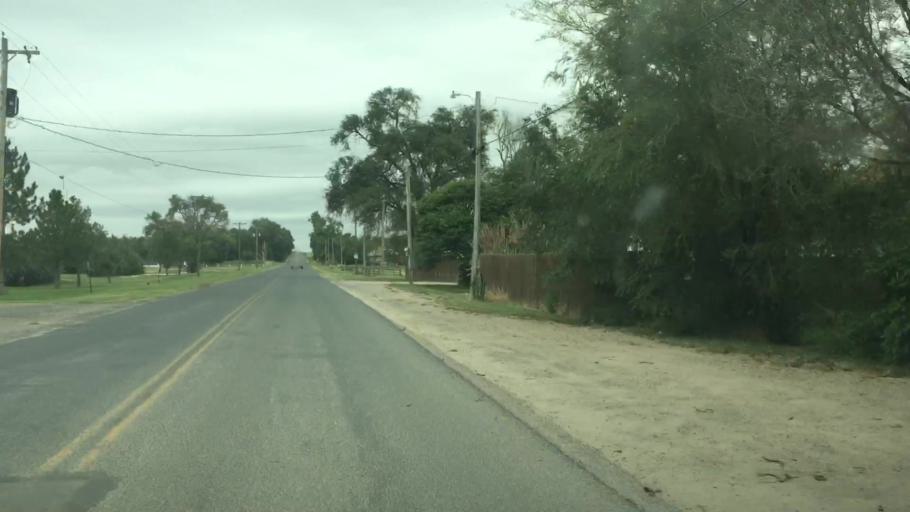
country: US
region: Kansas
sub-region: Hamilton County
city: Syracuse
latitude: 38.0541
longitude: -102.1185
